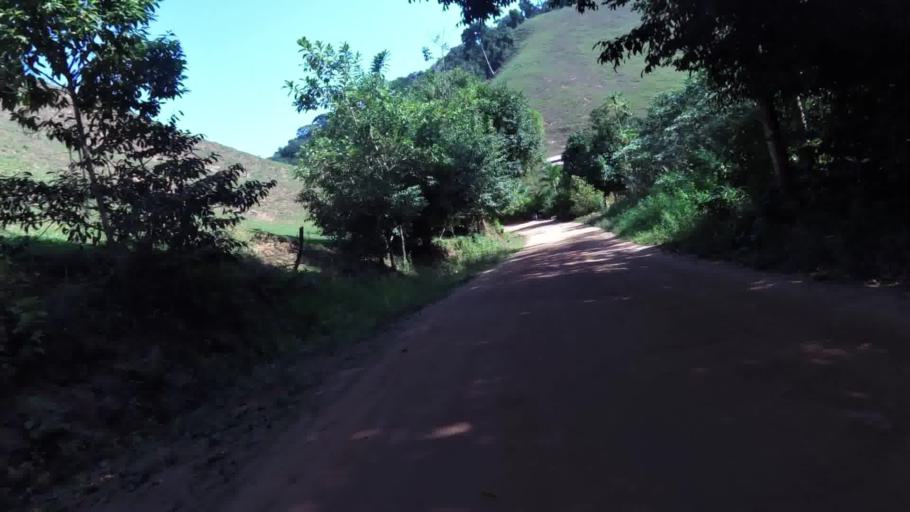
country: BR
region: Espirito Santo
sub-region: Alfredo Chaves
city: Alfredo Chaves
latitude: -20.5752
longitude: -40.7911
